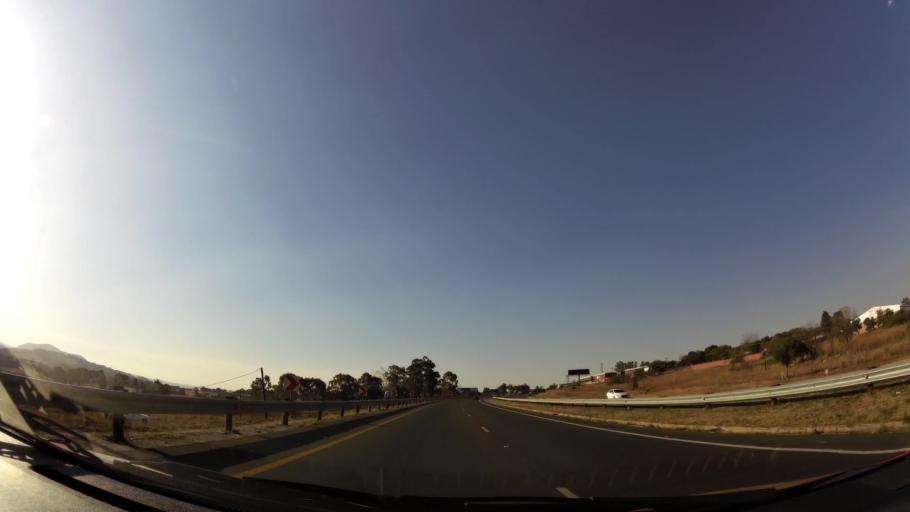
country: ZA
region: Gauteng
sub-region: West Rand District Municipality
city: Muldersdriseloop
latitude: -26.0271
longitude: 27.8503
